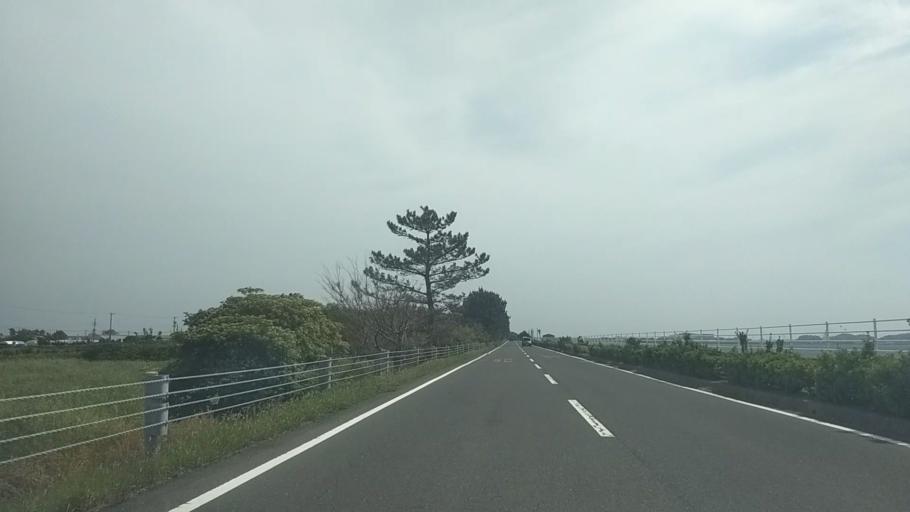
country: JP
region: Shizuoka
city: Kosai-shi
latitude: 34.7188
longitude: 137.5858
